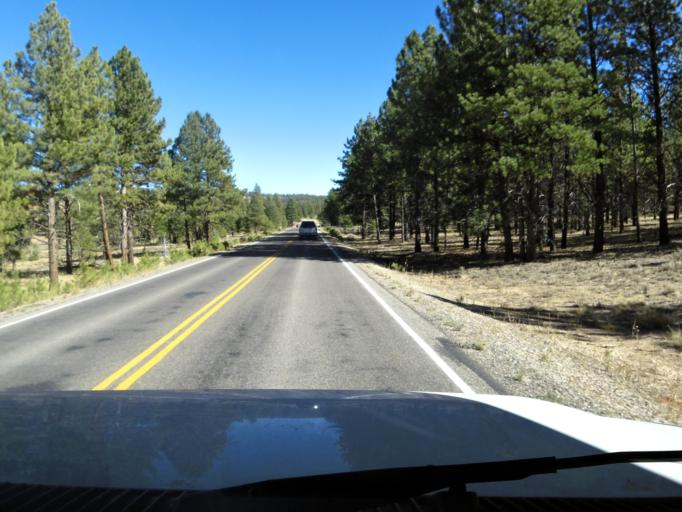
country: US
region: Utah
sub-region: Garfield County
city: Panguitch
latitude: 37.6070
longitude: -112.1952
